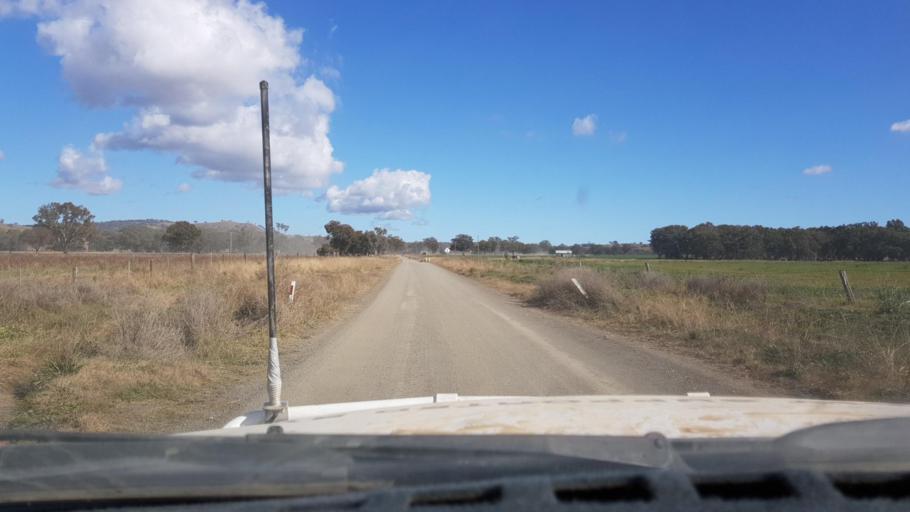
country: AU
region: New South Wales
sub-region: Tamworth Municipality
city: Manilla
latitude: -30.5848
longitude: 150.4858
